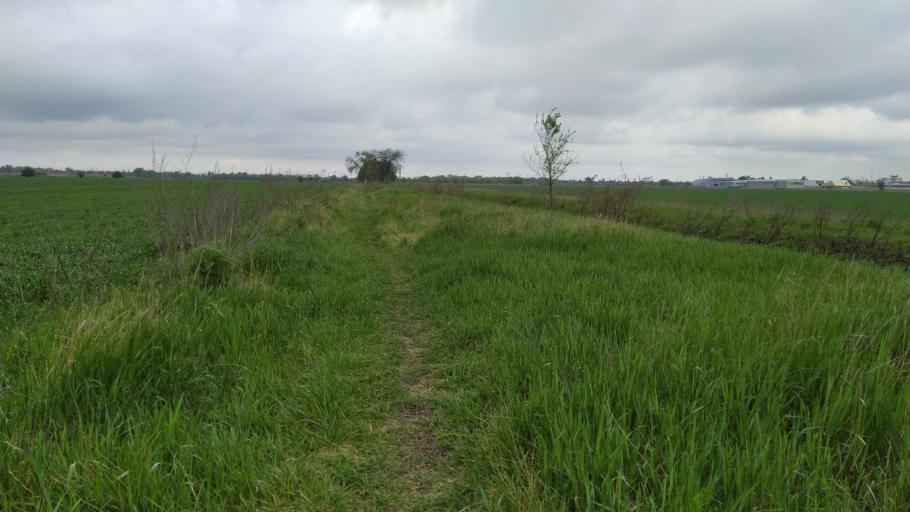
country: RU
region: Rostov
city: Bataysk
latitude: 47.1237
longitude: 39.7288
